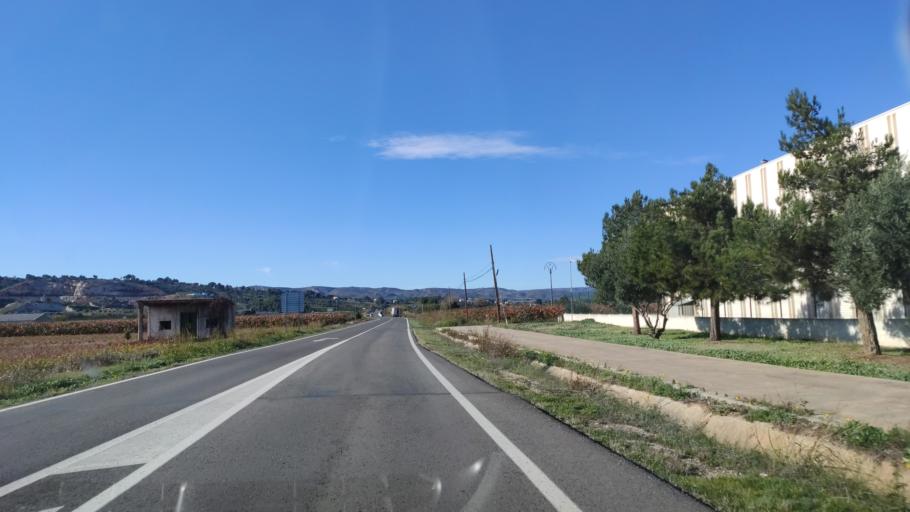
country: ES
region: Valencia
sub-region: Provincia de Valencia
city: Alberic
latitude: 39.1208
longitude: -0.5399
